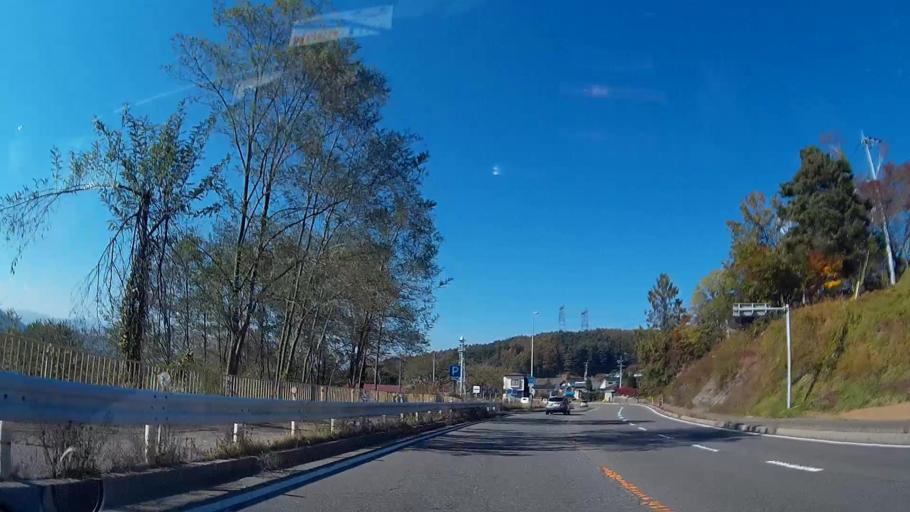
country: JP
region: Nagano
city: Shiojiri
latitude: 36.0939
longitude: 138.0141
